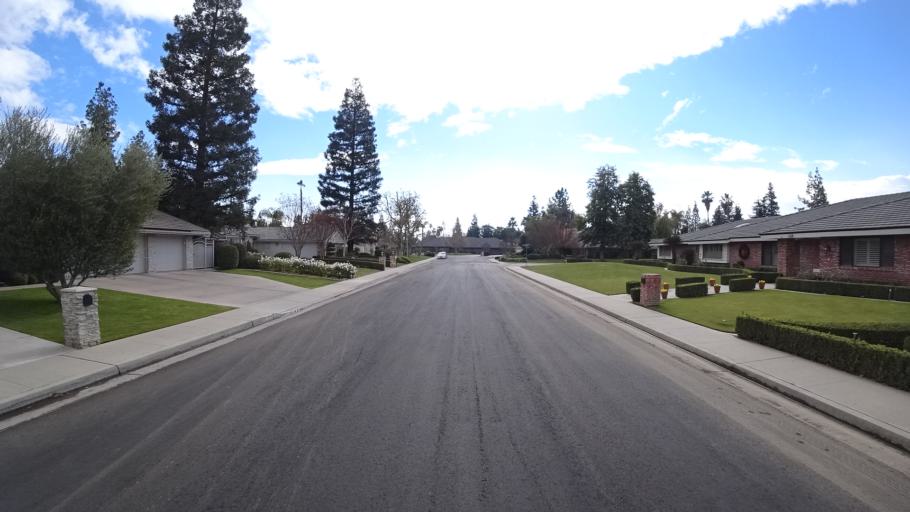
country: US
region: California
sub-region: Kern County
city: Greenacres
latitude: 35.3441
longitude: -119.0897
